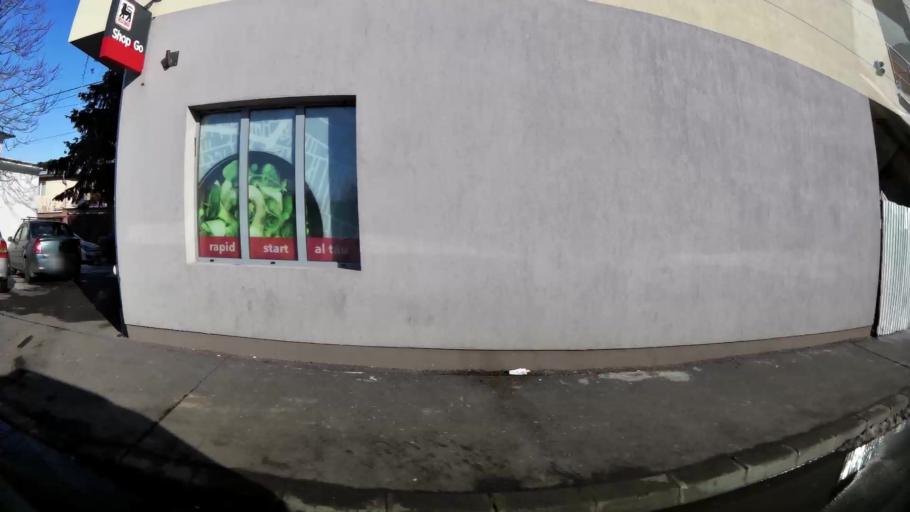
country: RO
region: Ilfov
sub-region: Comuna Fundeni-Dobroesti
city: Fundeni
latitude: 44.4792
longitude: 26.1433
